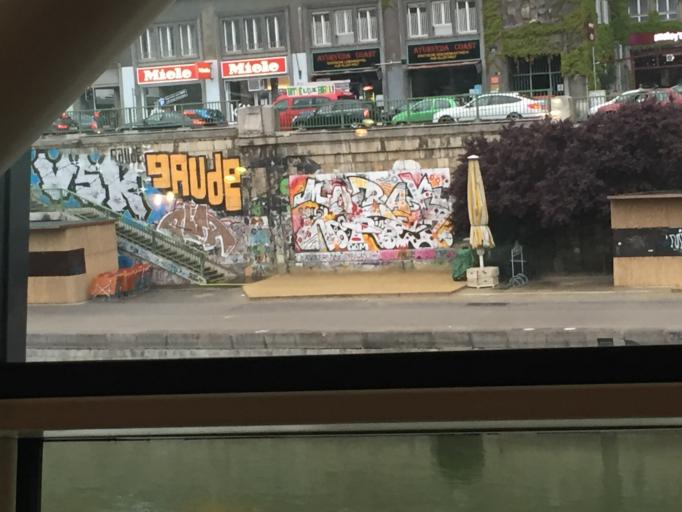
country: AT
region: Vienna
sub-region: Wien Stadt
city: Vienna
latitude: 48.2123
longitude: 16.3779
